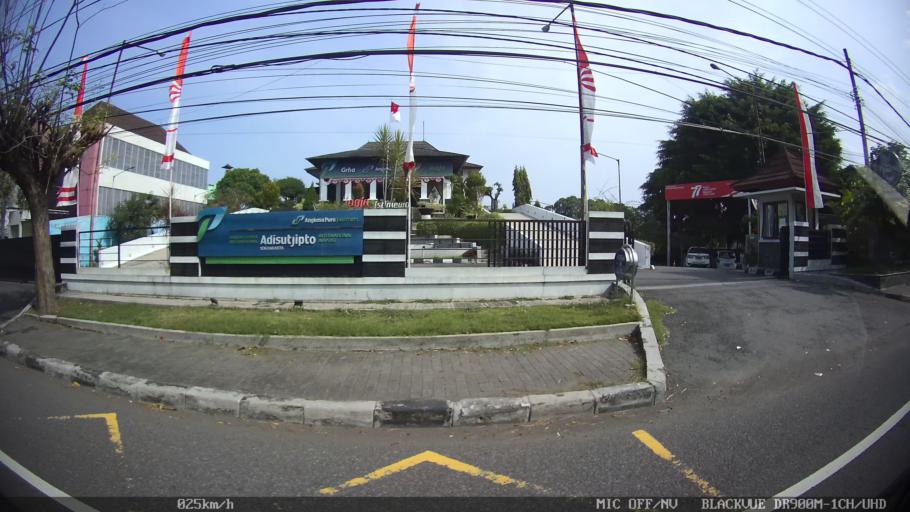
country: ID
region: Daerah Istimewa Yogyakarta
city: Depok
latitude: -7.7831
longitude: 110.4354
